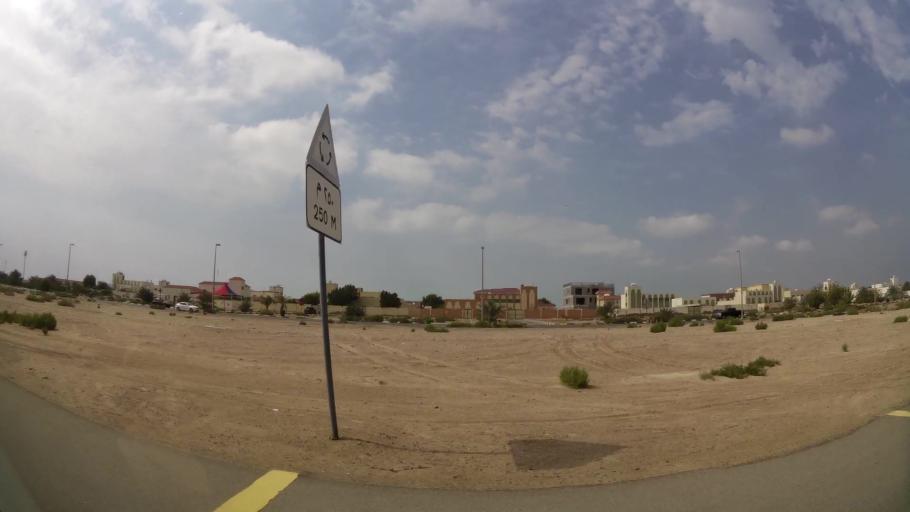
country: AE
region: Abu Dhabi
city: Abu Dhabi
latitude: 24.6018
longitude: 54.6505
